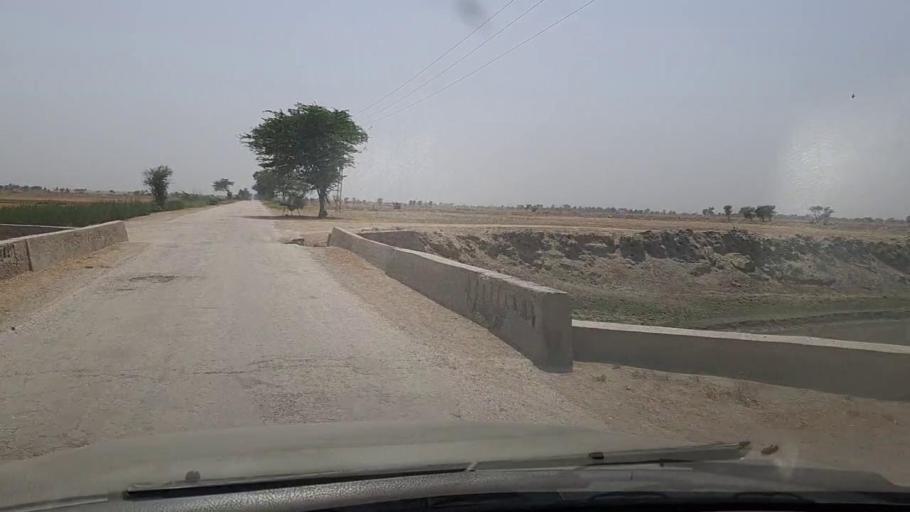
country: PK
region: Sindh
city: Miro Khan
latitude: 27.7085
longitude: 68.0639
